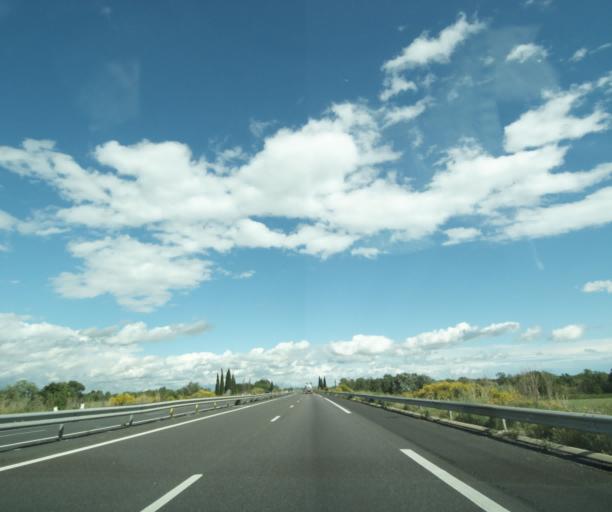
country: FR
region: Languedoc-Roussillon
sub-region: Departement du Gard
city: Bellegarde
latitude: 43.7324
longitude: 4.4729
